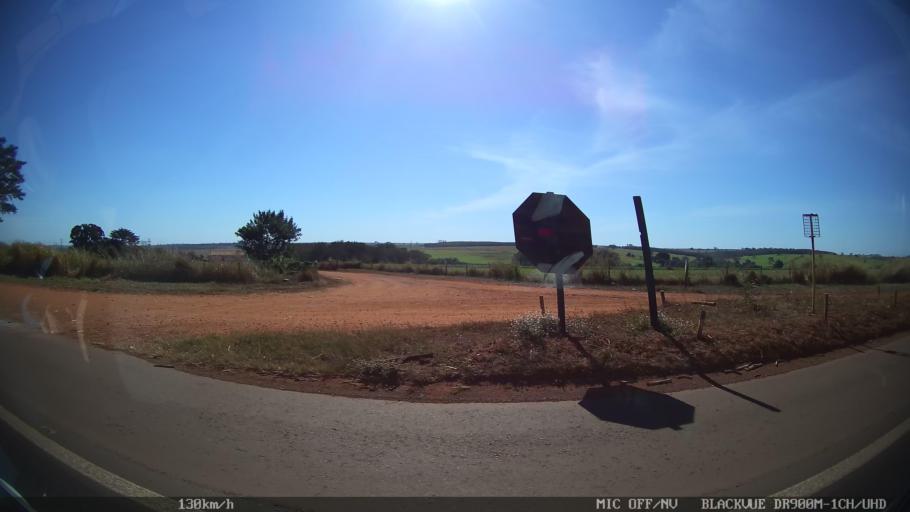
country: BR
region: Sao Paulo
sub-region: Olimpia
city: Olimpia
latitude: -20.6807
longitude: -48.8960
